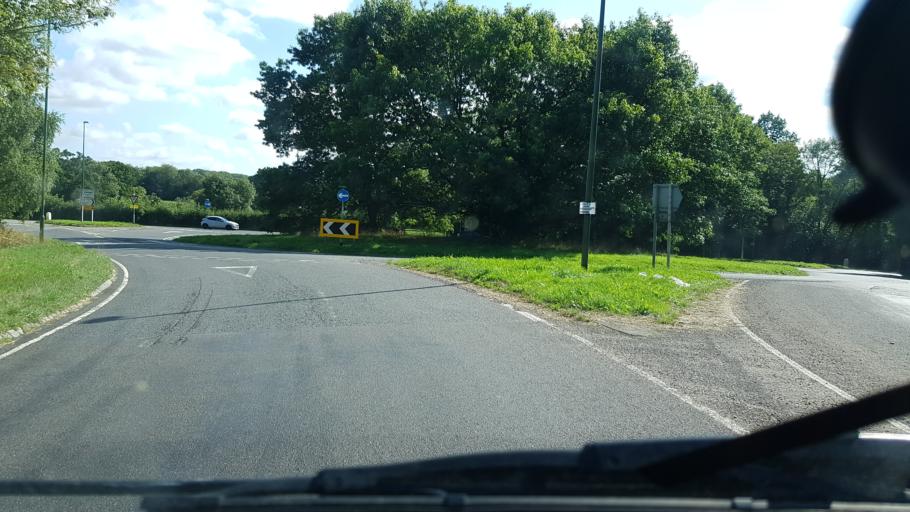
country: GB
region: England
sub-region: Surrey
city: Ockley
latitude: 51.0899
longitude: -0.3870
